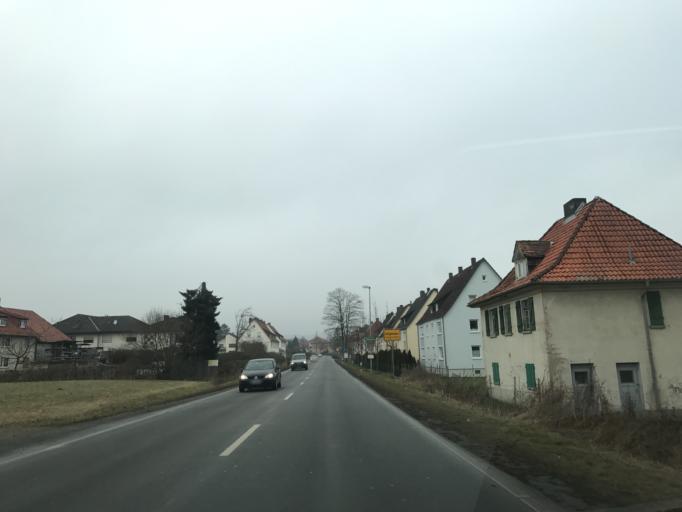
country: DE
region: Hesse
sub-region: Regierungsbezirk Kassel
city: Hofgeismar
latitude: 51.4858
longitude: 9.3871
